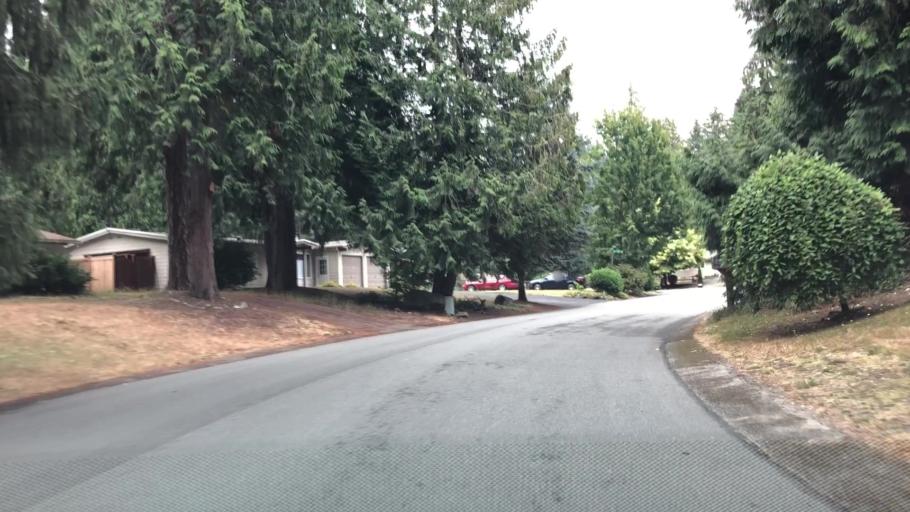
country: US
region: Washington
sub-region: King County
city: Cottage Lake
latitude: 47.7552
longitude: -122.0732
